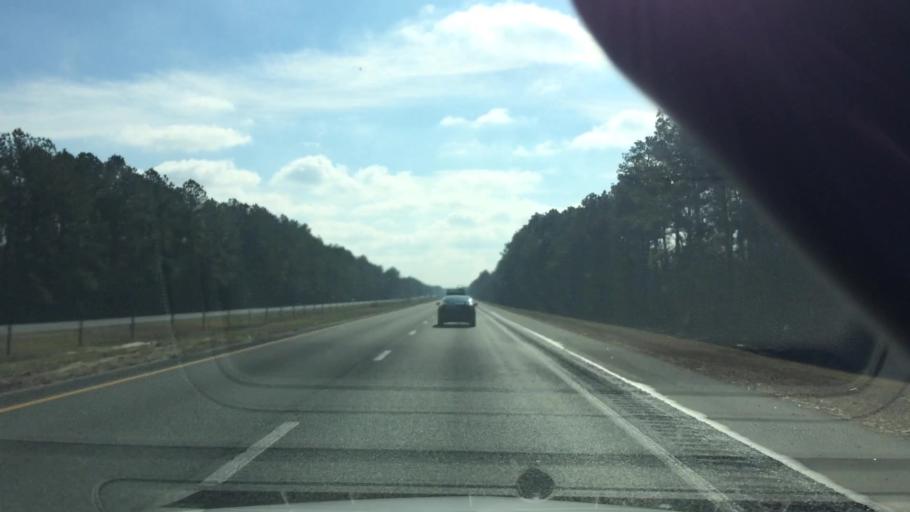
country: US
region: North Carolina
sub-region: Duplin County
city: Wallace
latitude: 34.7257
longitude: -77.9452
